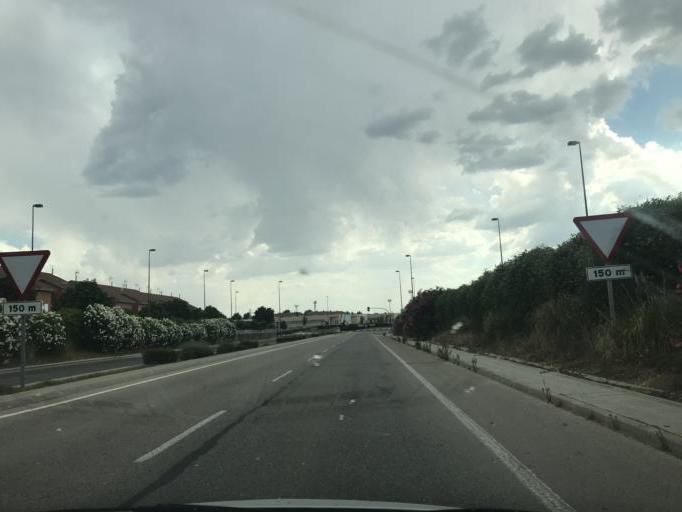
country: ES
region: Madrid
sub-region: Provincia de Madrid
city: Paracuellos de Jarama
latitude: 40.5072
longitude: -3.5180
